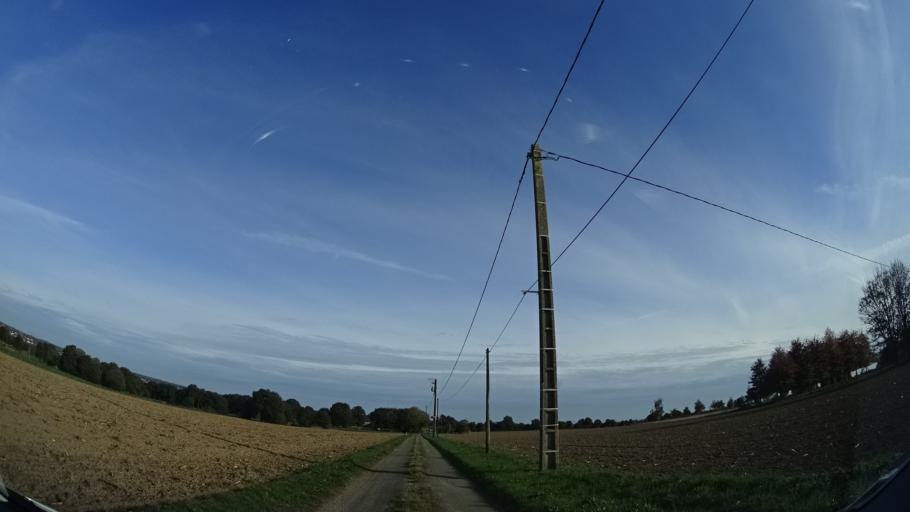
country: FR
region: Brittany
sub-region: Departement d'Ille-et-Vilaine
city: Geveze
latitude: 48.2085
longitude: -1.8256
